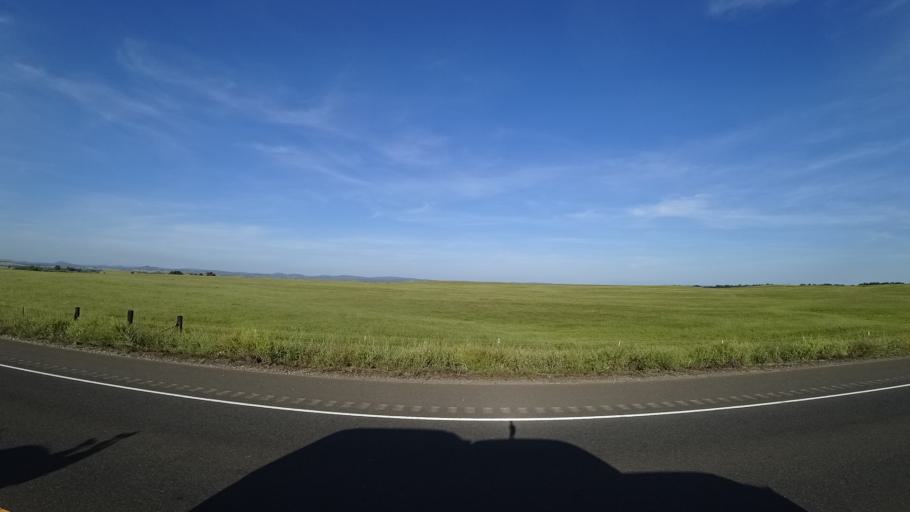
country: US
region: California
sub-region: Placer County
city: Sheridan
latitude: 38.9493
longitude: -121.3559
